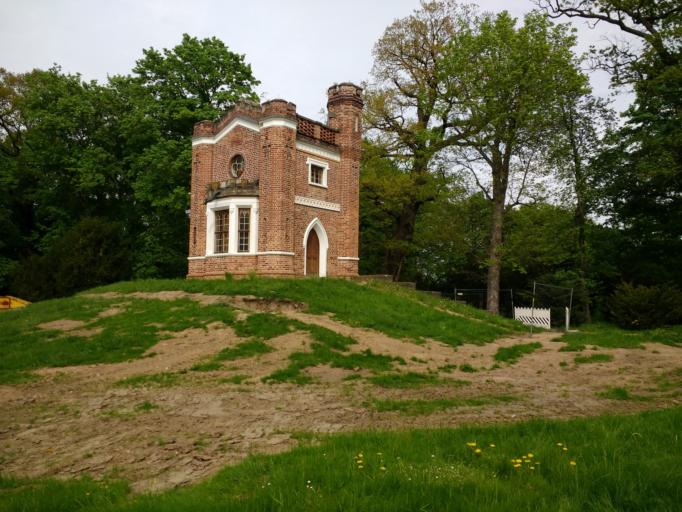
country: DE
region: Saxony-Anhalt
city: Dessau
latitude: 51.8494
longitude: 12.2761
